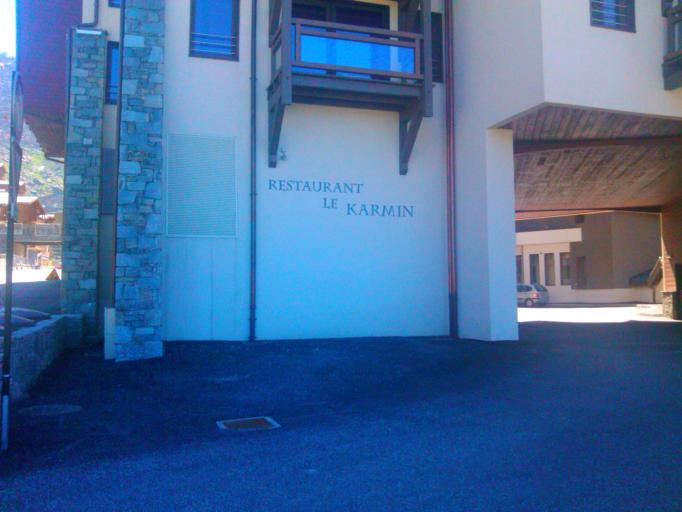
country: FR
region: Rhone-Alpes
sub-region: Departement de la Savoie
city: Val Thorens
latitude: 45.2989
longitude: 6.5755
